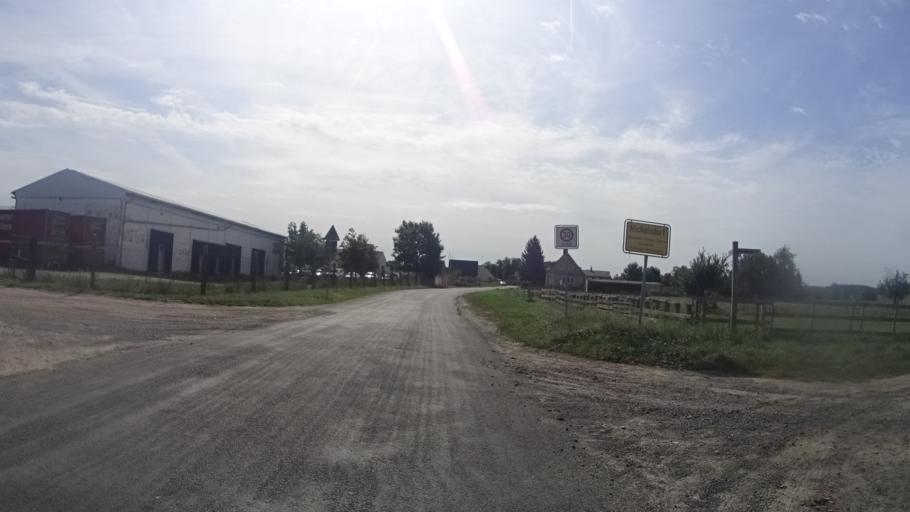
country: DE
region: Brandenburg
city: Golzow
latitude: 52.3107
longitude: 12.6954
